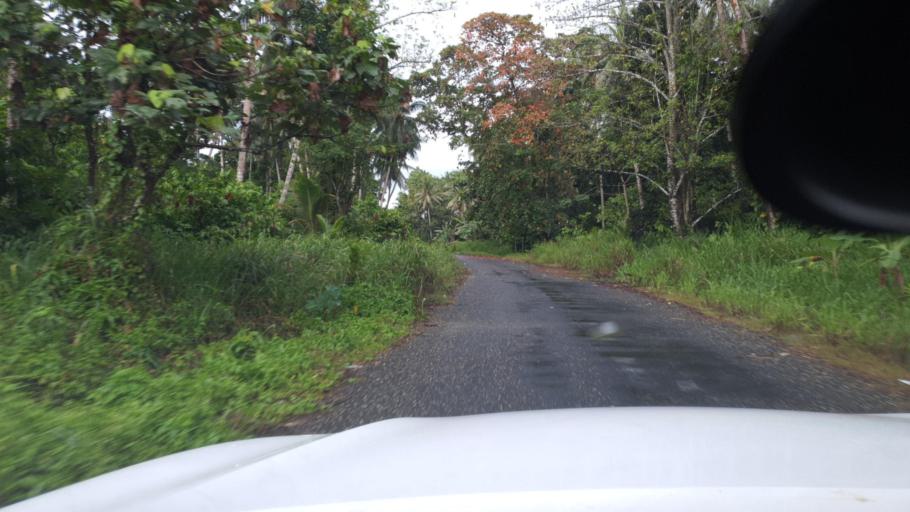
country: SB
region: Guadalcanal
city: Honiara
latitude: -9.4805
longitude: 160.3565
